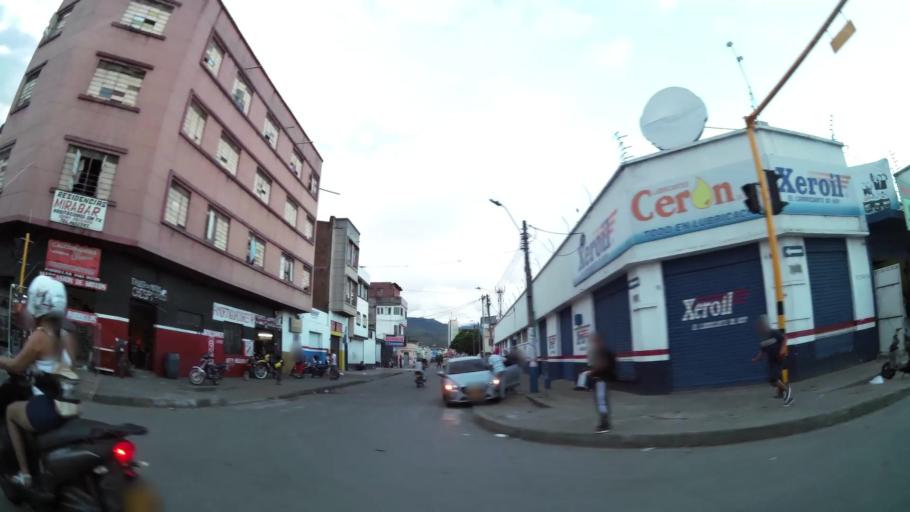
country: CO
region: Valle del Cauca
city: Cali
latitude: 3.4434
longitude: -76.5234
